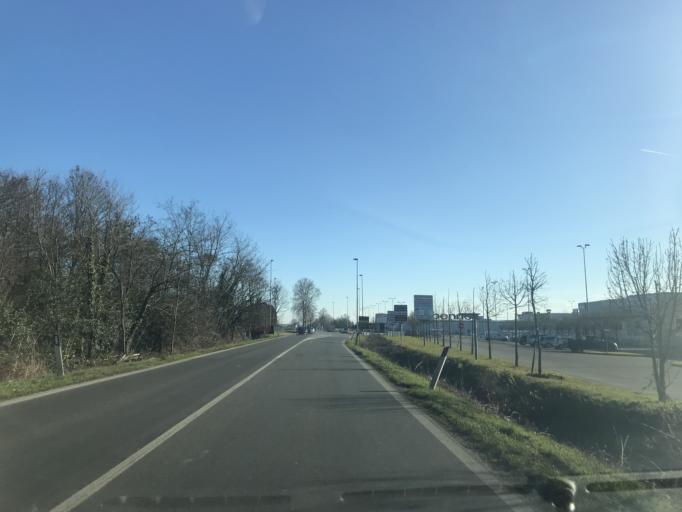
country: IT
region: Lombardy
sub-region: Provincia di Lodi
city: San Martino in Strada
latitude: 45.2846
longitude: 9.5368
